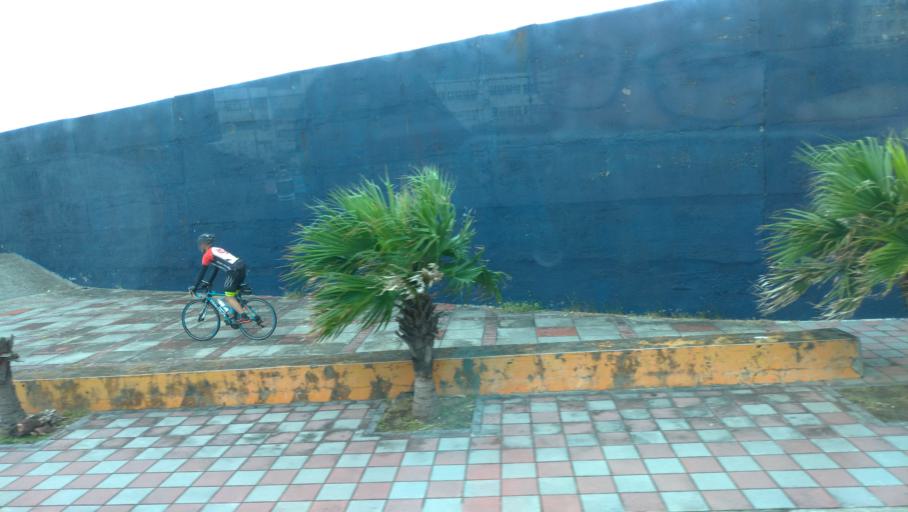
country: TW
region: Taiwan
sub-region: Keelung
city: Keelung
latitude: 25.1513
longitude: 121.7776
